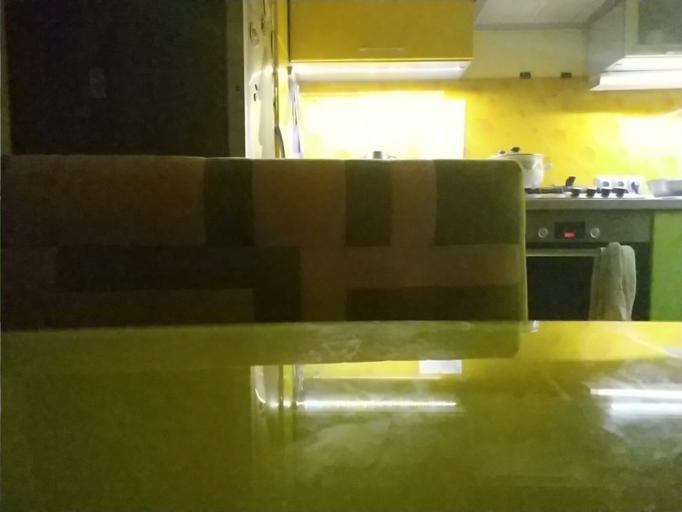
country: RU
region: Republic of Karelia
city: Pyaozerskiy
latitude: 65.6026
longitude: 30.5633
